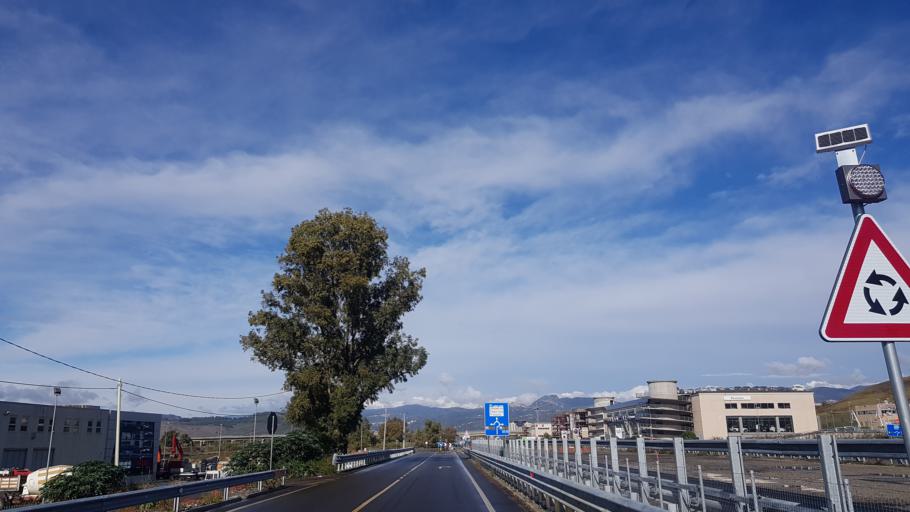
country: IT
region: Calabria
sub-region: Provincia di Catanzaro
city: Roccelletta
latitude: 38.8434
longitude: 16.5843
